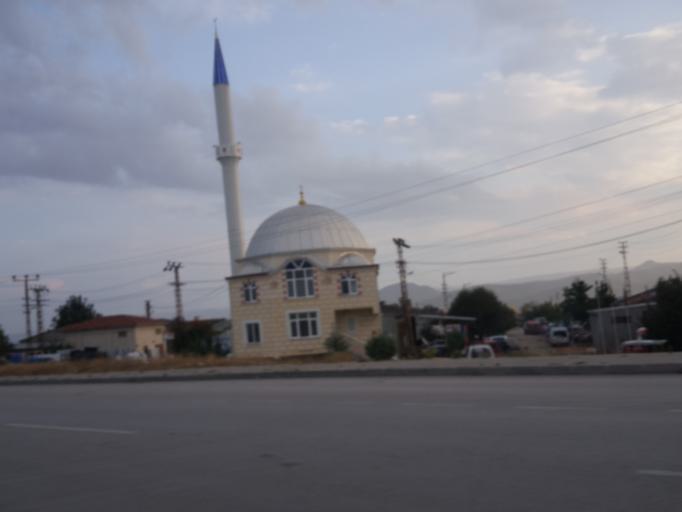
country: TR
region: Amasya
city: Gumushacikoy
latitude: 40.8737
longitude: 35.2409
